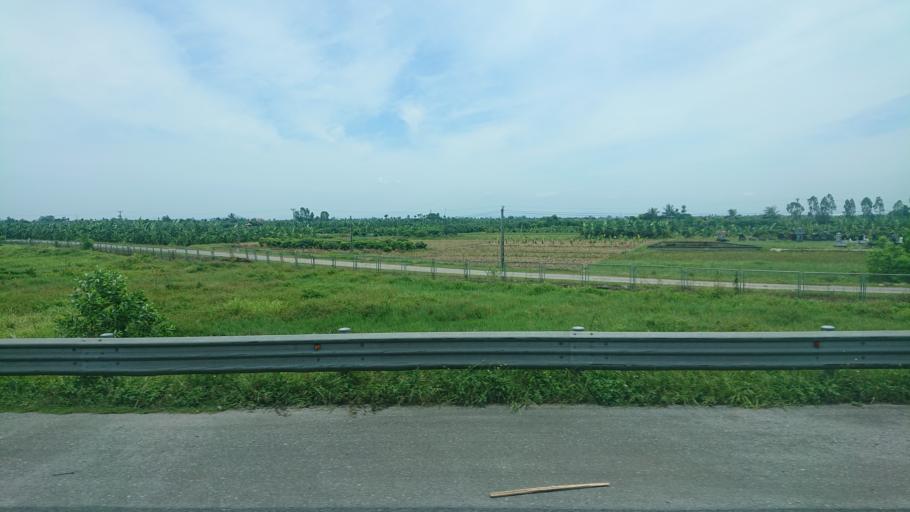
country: VN
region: Hai Phong
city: An Lao
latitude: 20.8143
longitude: 106.4958
